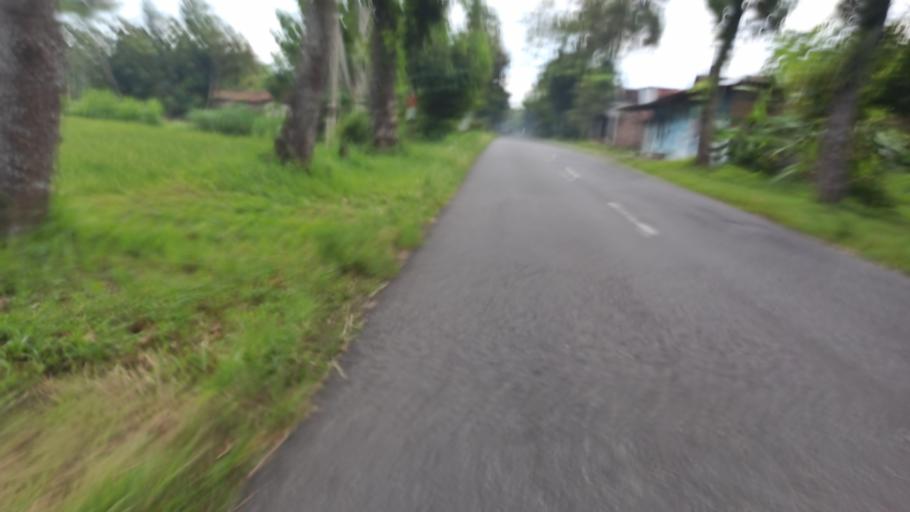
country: ID
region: Daerah Istimewa Yogyakarta
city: Sleman
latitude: -7.6982
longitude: 110.2909
